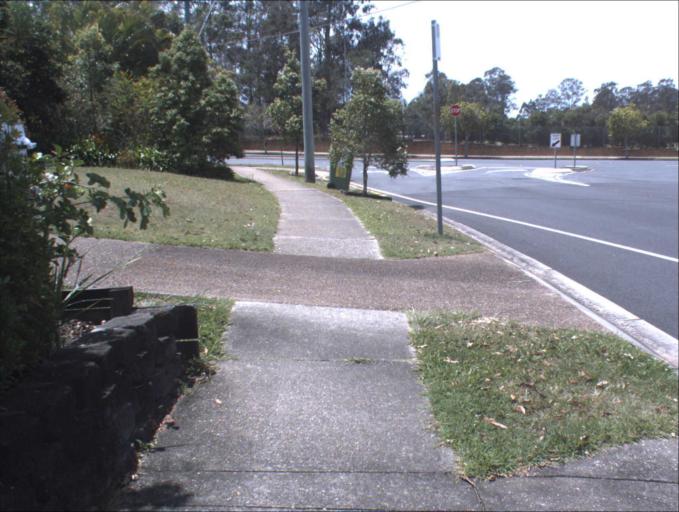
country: AU
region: Queensland
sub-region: Logan
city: Slacks Creek
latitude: -27.6387
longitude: 153.1460
